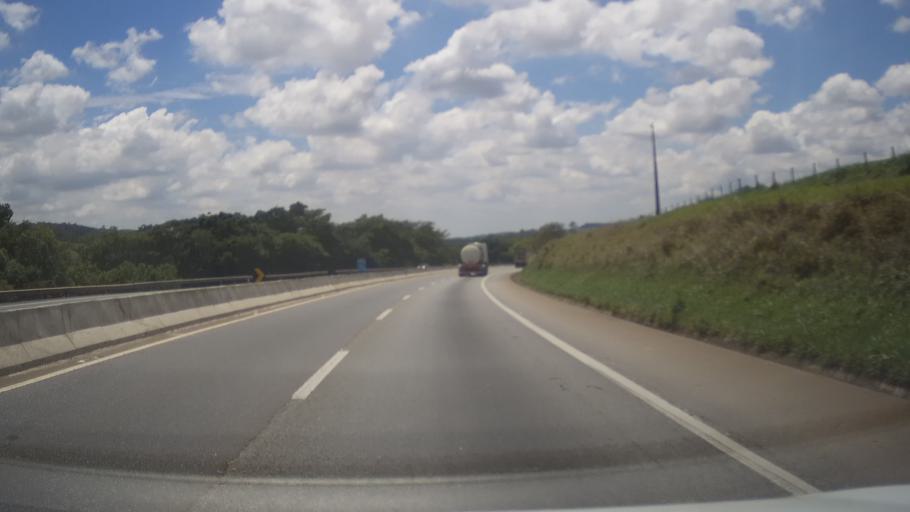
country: BR
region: Minas Gerais
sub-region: Campanha
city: Campanha
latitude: -21.8019
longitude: -45.4711
